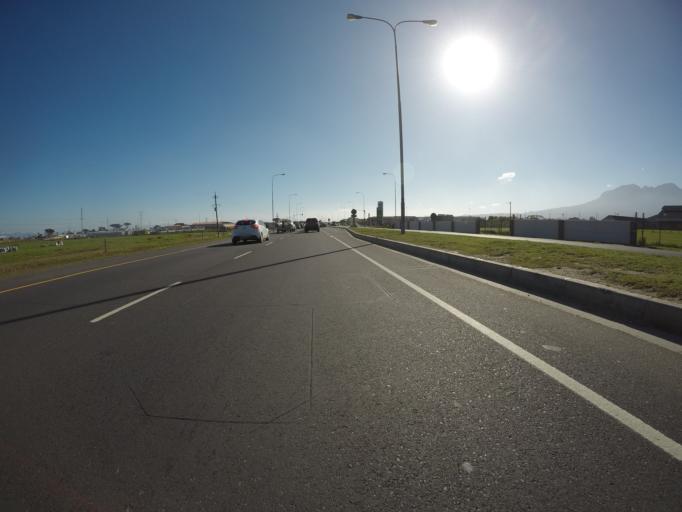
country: ZA
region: Western Cape
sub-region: Overberg District Municipality
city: Grabouw
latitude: -34.1091
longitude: 18.8623
